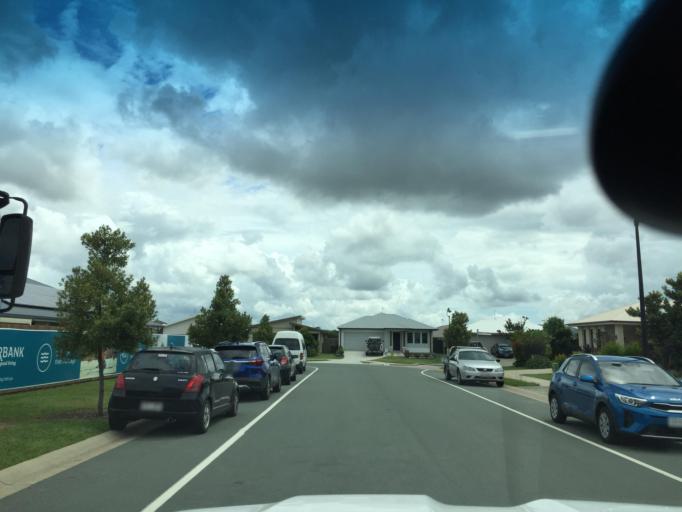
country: AU
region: Queensland
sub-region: Moreton Bay
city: Caboolture South
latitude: -27.0953
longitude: 152.9647
